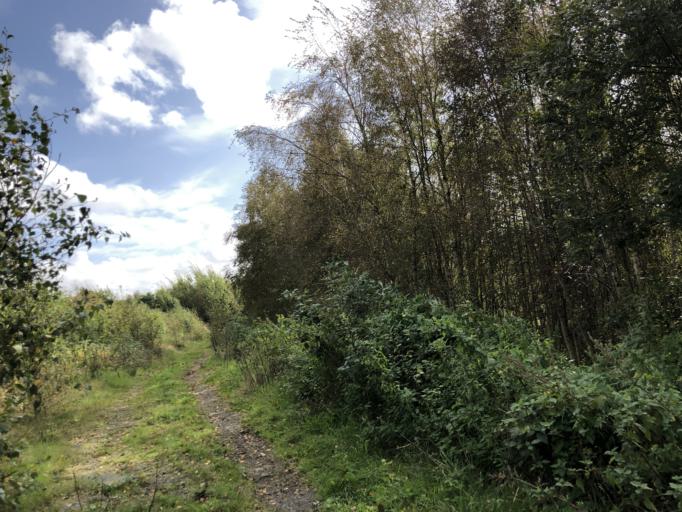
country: SE
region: Vaestra Goetaland
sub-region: Goteborg
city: Majorna
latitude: 57.7628
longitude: 11.8698
